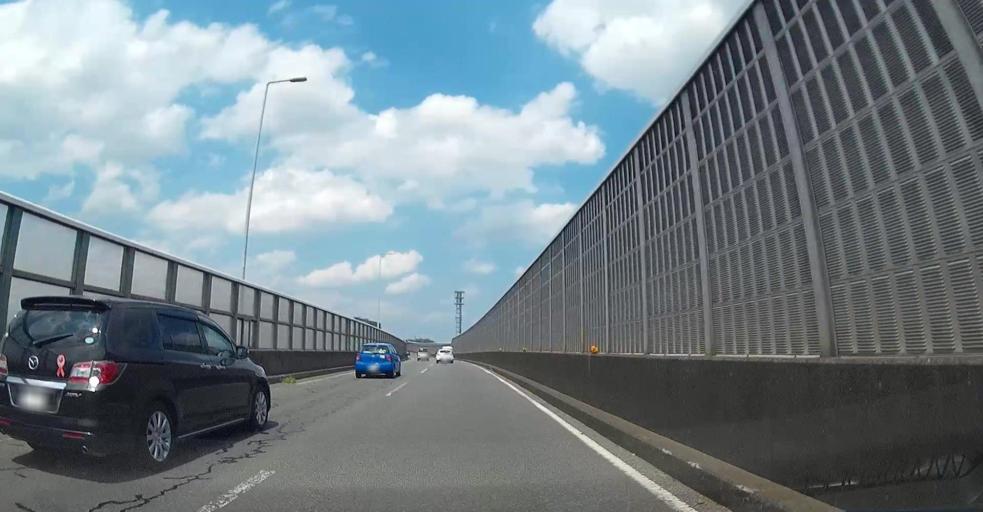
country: JP
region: Saitama
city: Kamifukuoka
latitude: 35.9193
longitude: 139.5584
